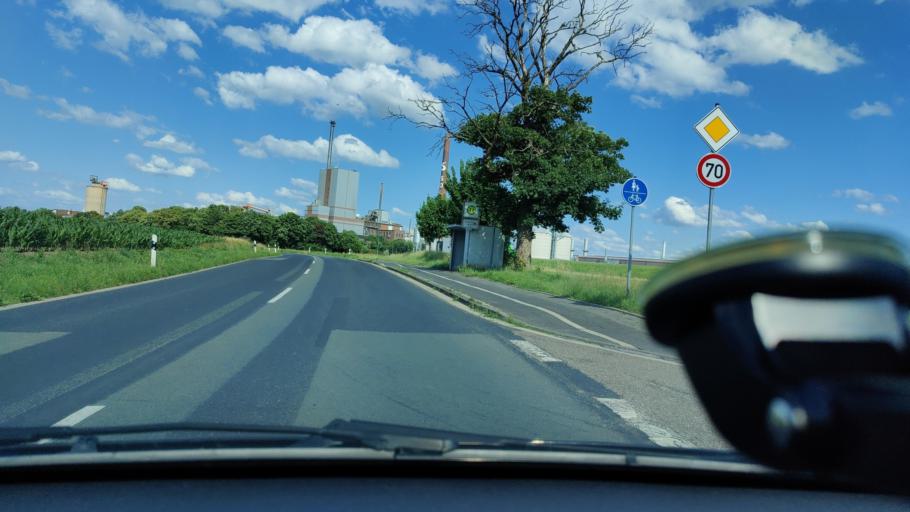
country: DE
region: North Rhine-Westphalia
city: Rheinberg
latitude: 51.5642
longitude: 6.5706
